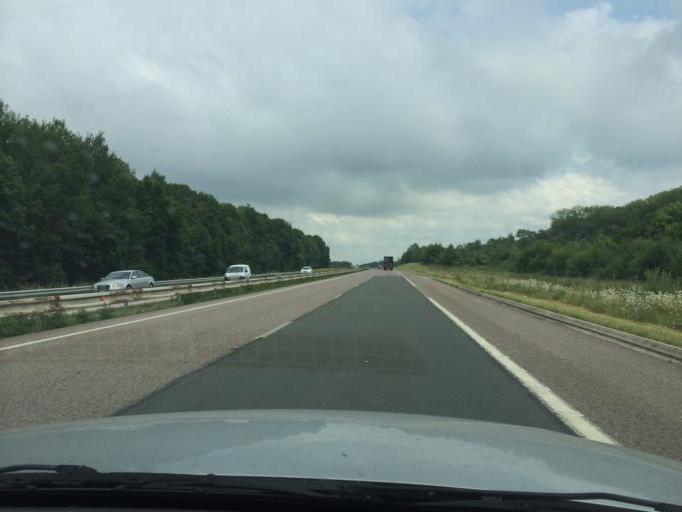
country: FR
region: Picardie
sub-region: Departement de l'Aisne
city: Crezancy
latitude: 49.1103
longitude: 3.4866
